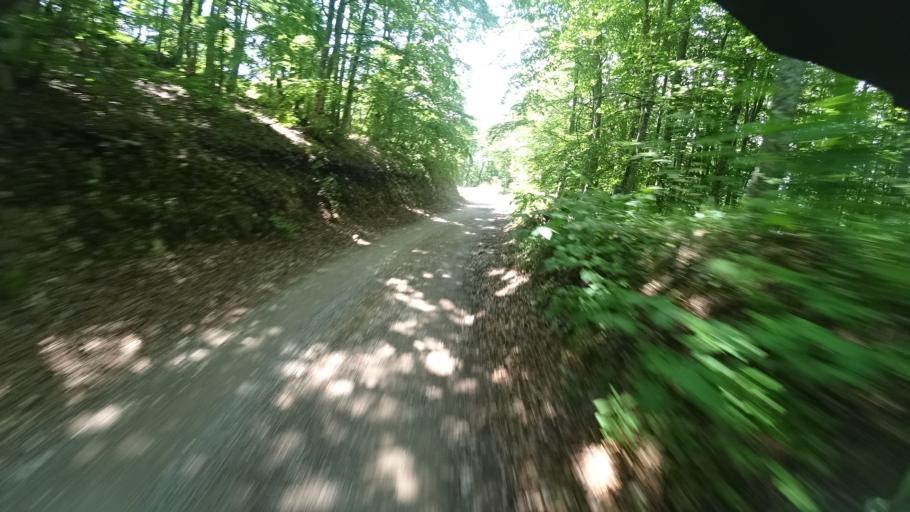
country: BA
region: Federation of Bosnia and Herzegovina
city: Orasac
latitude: 44.5761
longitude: 15.8520
